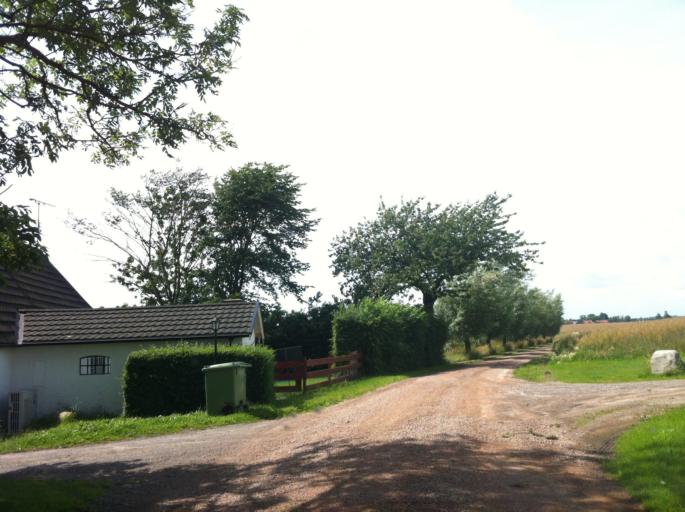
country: SE
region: Skane
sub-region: Skurups Kommun
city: Skurup
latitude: 55.4488
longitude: 13.4345
